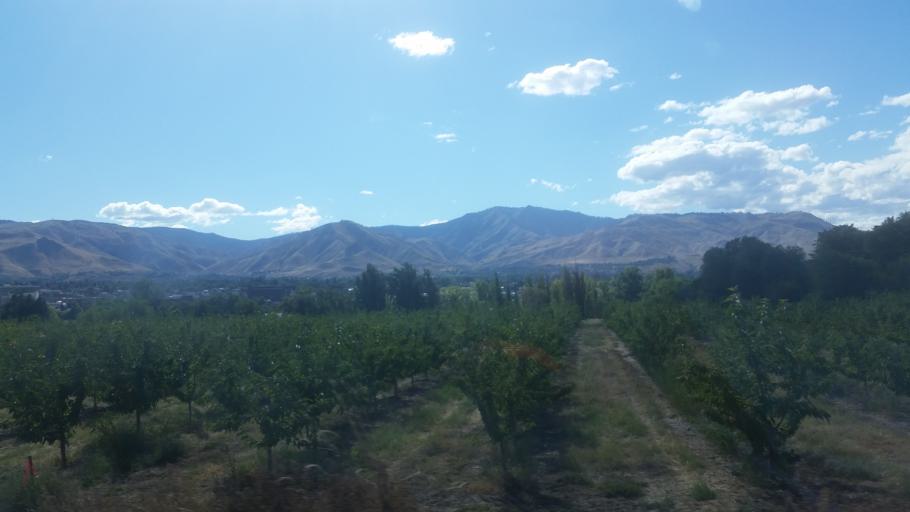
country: US
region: Washington
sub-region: Chelan County
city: Wenatchee
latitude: 47.4329
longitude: -120.2976
